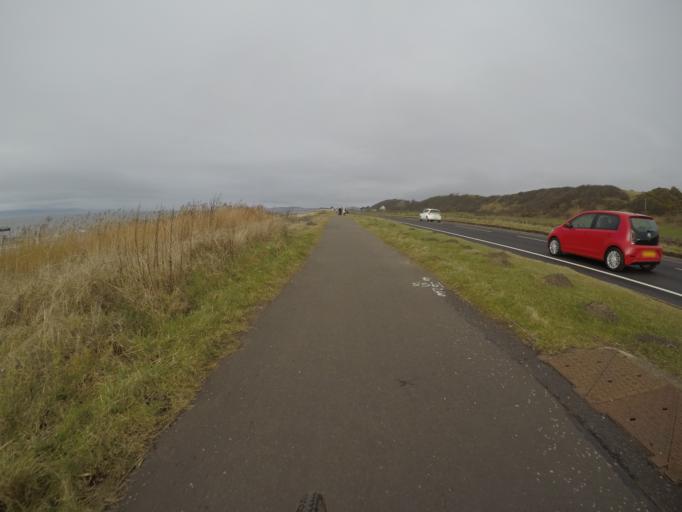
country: GB
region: Scotland
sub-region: North Ayrshire
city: West Kilbride
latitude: 55.6624
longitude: -4.8332
